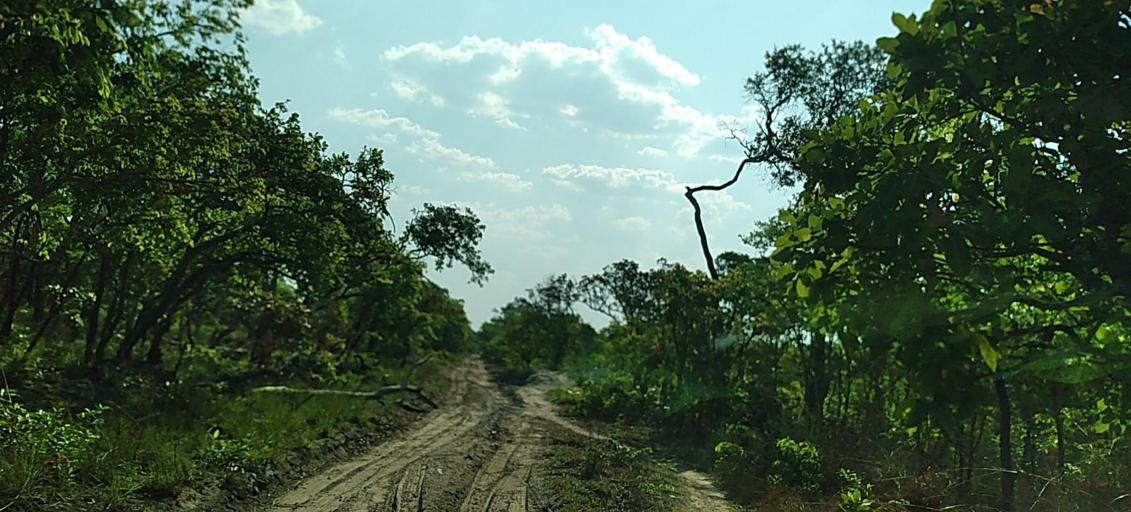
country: ZM
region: North-Western
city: Mwinilunga
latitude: -11.3077
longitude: 24.7889
